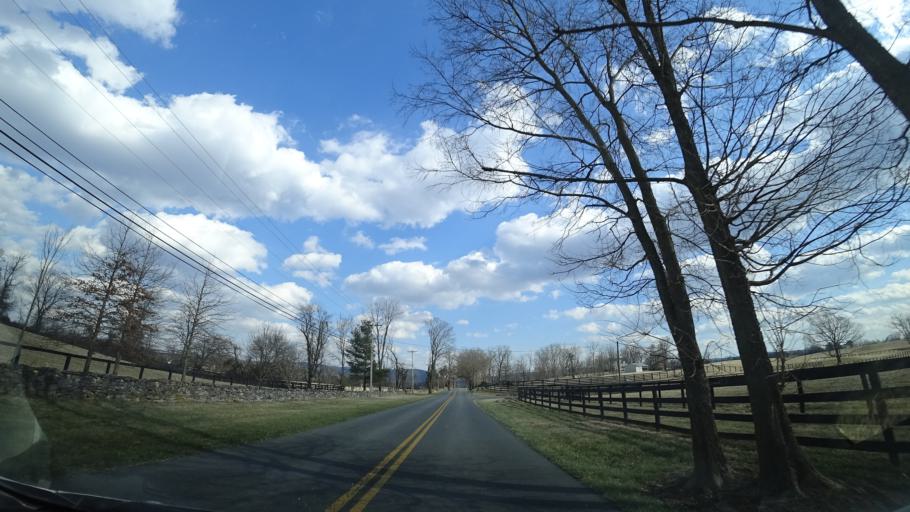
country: US
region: Virginia
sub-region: Warren County
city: Shenandoah Farms
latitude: 39.0603
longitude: -78.0251
